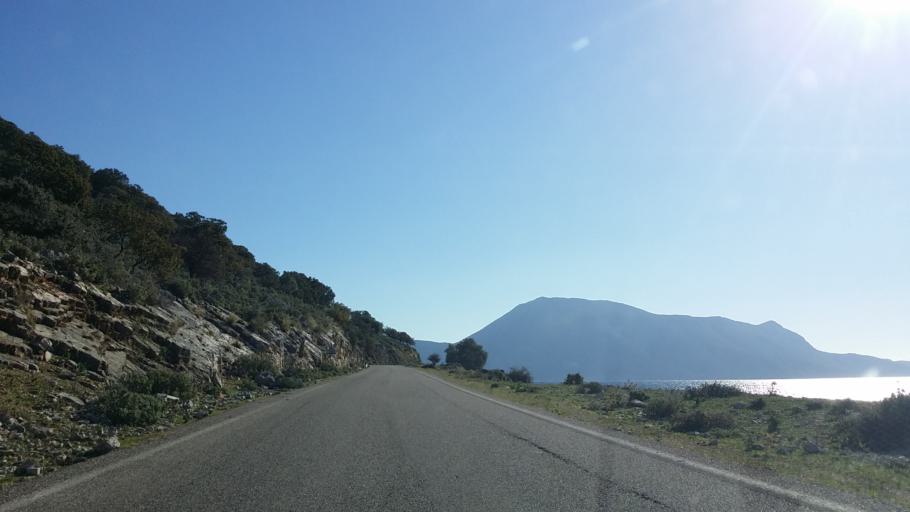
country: GR
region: West Greece
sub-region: Nomos Aitolias kai Akarnanias
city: Kandila
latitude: 38.7032
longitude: 20.8979
